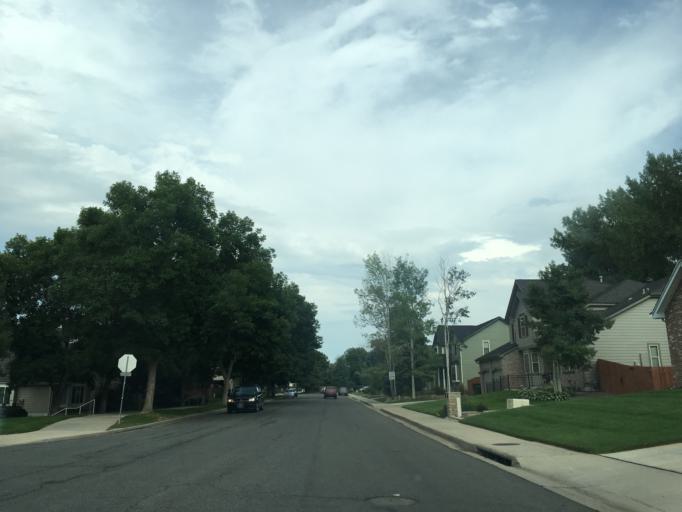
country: US
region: Colorado
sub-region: Jefferson County
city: Lakewood
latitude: 39.6740
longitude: -105.0575
